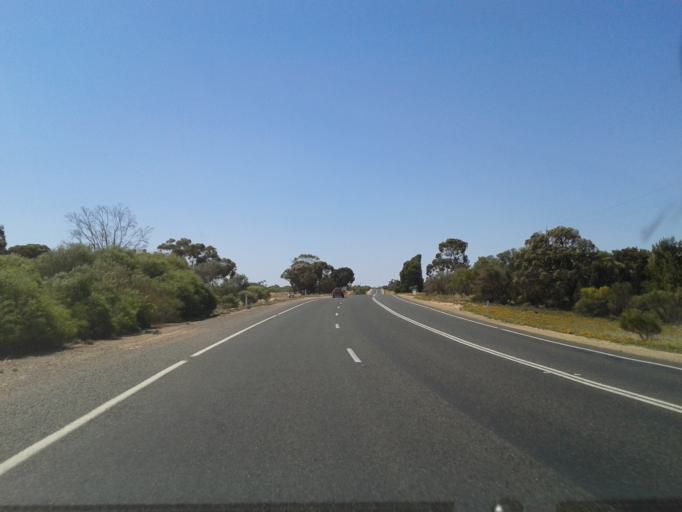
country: AU
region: South Australia
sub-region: Loxton Waikerie
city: Loxton
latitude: -34.3858
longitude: 140.6018
